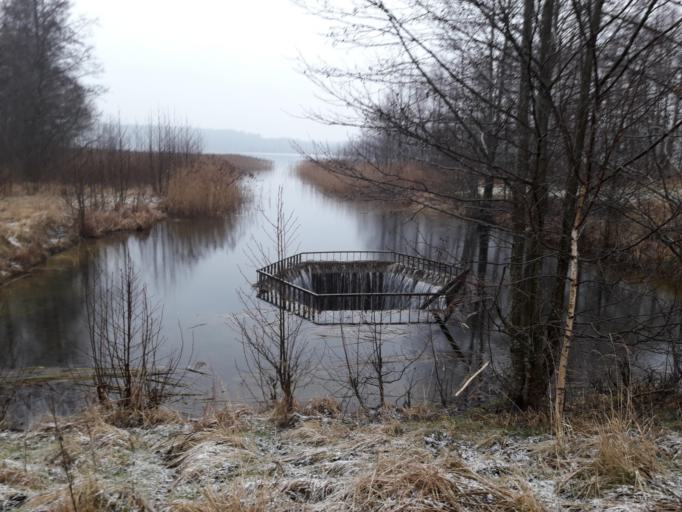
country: LT
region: Alytaus apskritis
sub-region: Alytaus rajonas
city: Daugai
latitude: 54.2308
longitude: 24.2584
